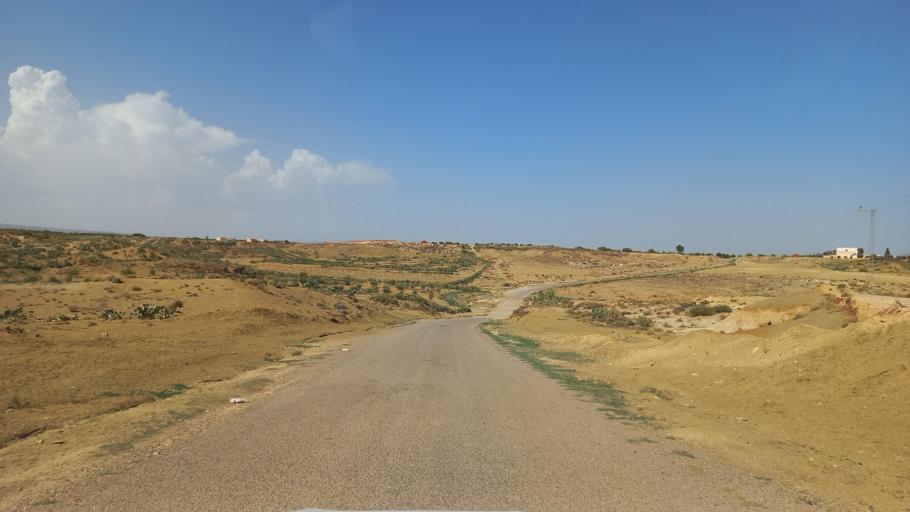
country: TN
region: Al Qasrayn
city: Kasserine
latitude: 35.2045
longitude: 9.0382
